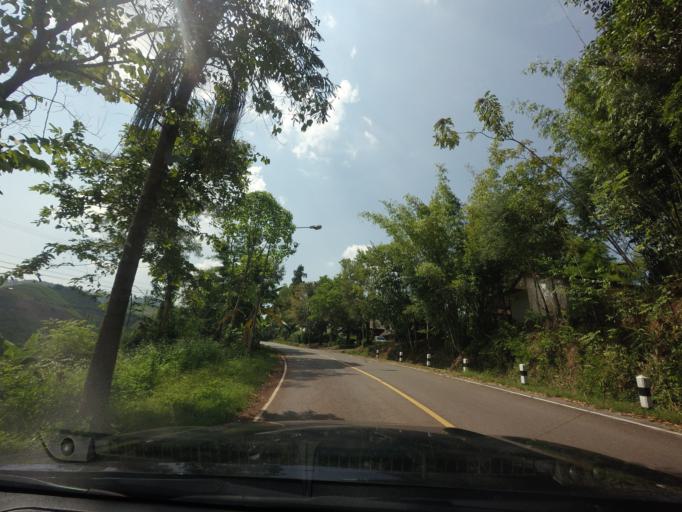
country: TH
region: Nan
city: Bo Kluea
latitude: 19.0112
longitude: 101.2002
